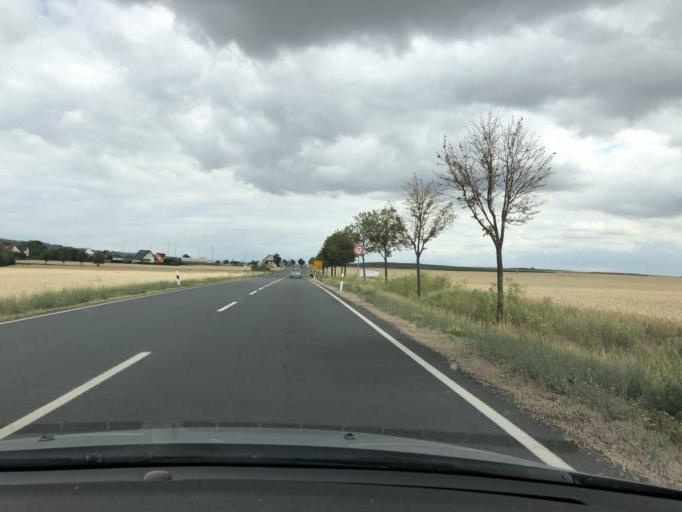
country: DE
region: Saxony-Anhalt
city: Erdeborn
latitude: 51.5000
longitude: 11.6215
